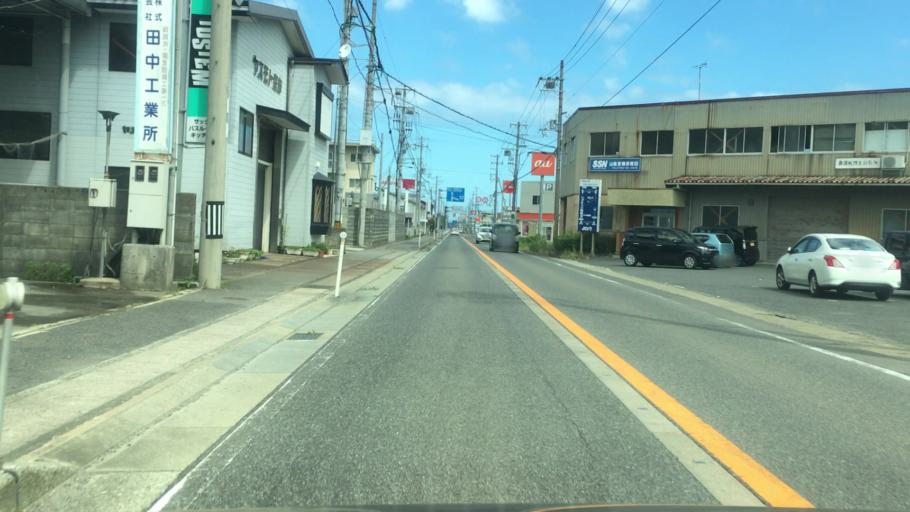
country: JP
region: Tottori
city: Tottori
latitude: 35.6129
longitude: 134.4679
